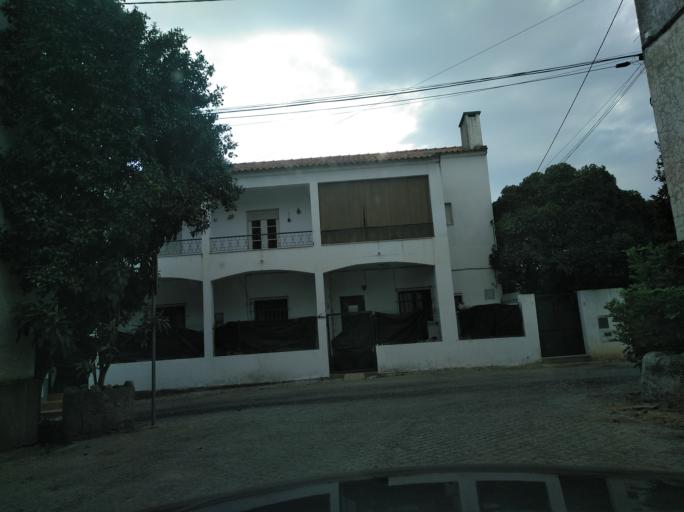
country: PT
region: Portalegre
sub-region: Elvas
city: Elvas
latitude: 38.8953
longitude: -7.1396
